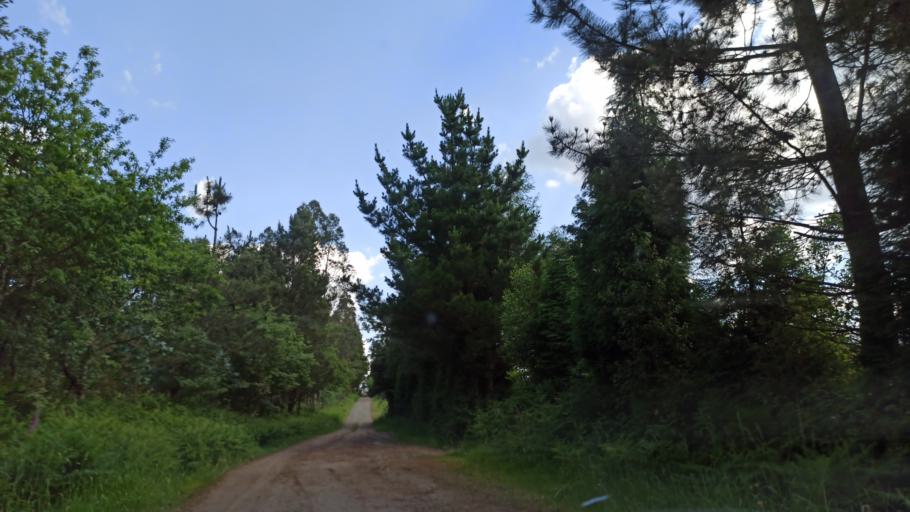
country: ES
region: Galicia
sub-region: Provincia da Coruna
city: Santa Comba
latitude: 43.0784
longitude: -8.7185
